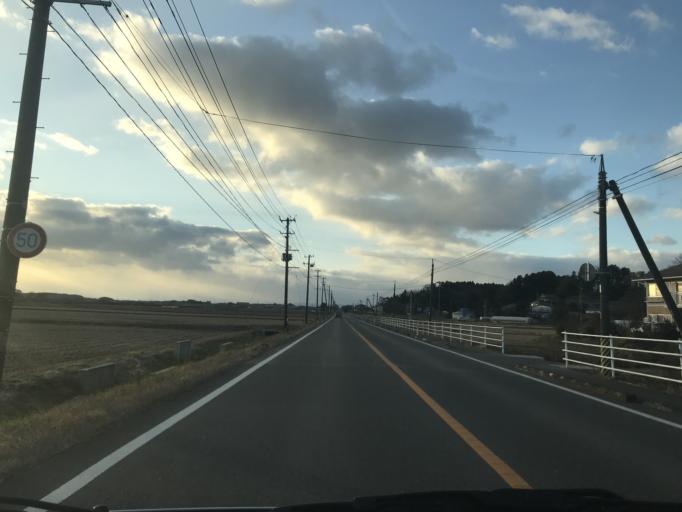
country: JP
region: Miyagi
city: Kogota
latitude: 38.6552
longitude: 141.0427
